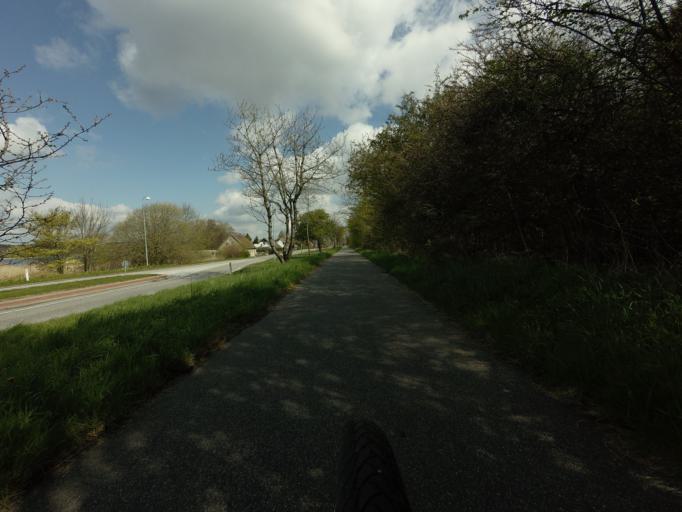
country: DK
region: North Denmark
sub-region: Mariagerfjord Kommune
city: Hadsund
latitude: 56.7000
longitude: 10.1140
